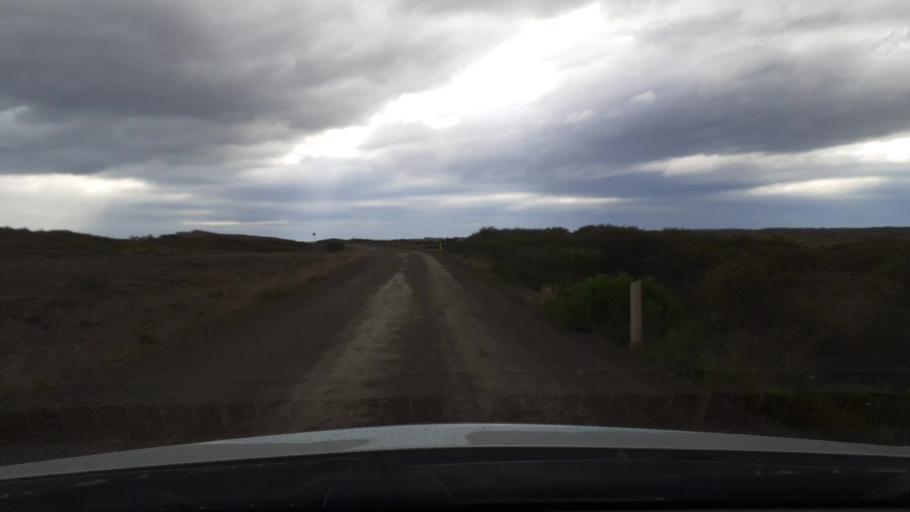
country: IS
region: West
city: Borgarnes
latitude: 64.5947
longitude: -21.9850
